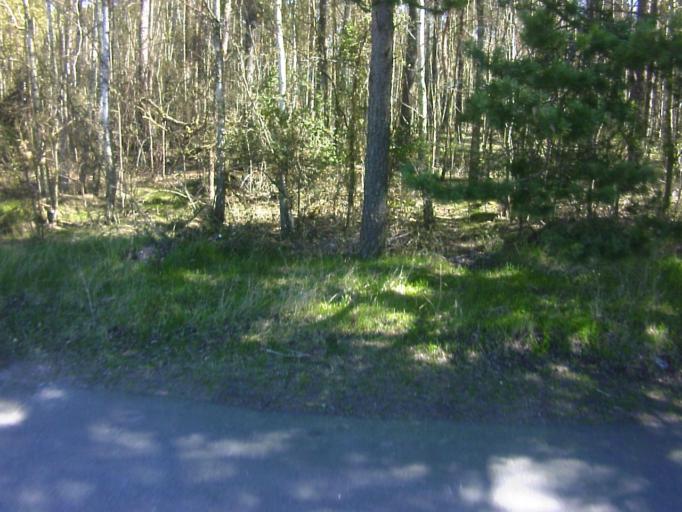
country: SE
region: Skane
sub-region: Kavlinge Kommun
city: Hofterup
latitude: 55.8098
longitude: 12.9853
